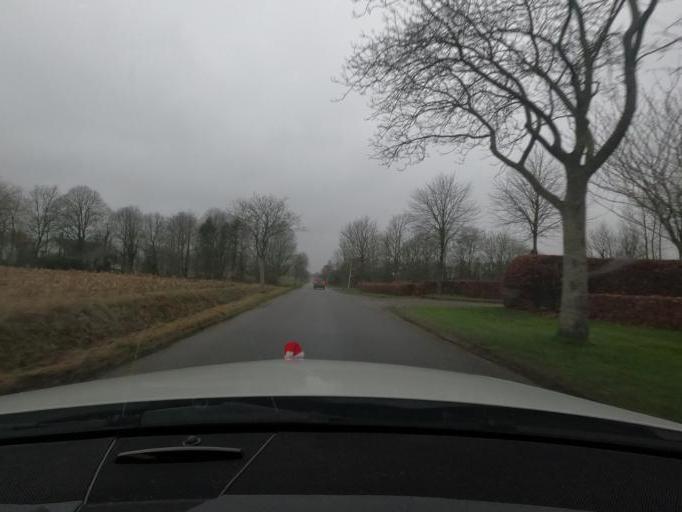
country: DK
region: South Denmark
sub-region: Haderslev Kommune
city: Haderslev
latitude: 55.1949
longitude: 9.4846
